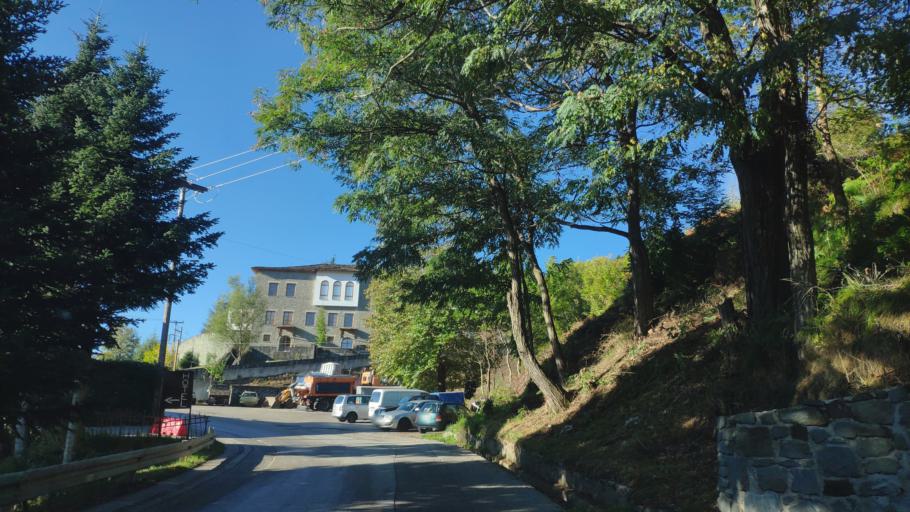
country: GR
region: Epirus
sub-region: Nomos Ioanninon
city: Metsovo
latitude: 39.7722
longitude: 21.1781
